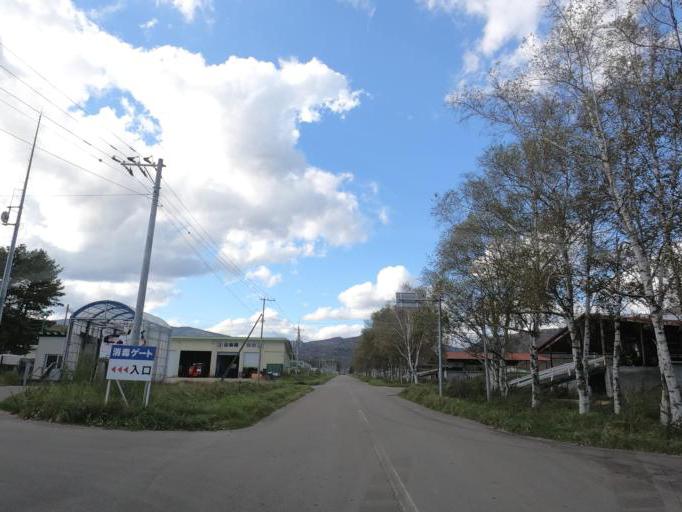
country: JP
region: Hokkaido
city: Otofuke
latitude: 43.2841
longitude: 143.2370
